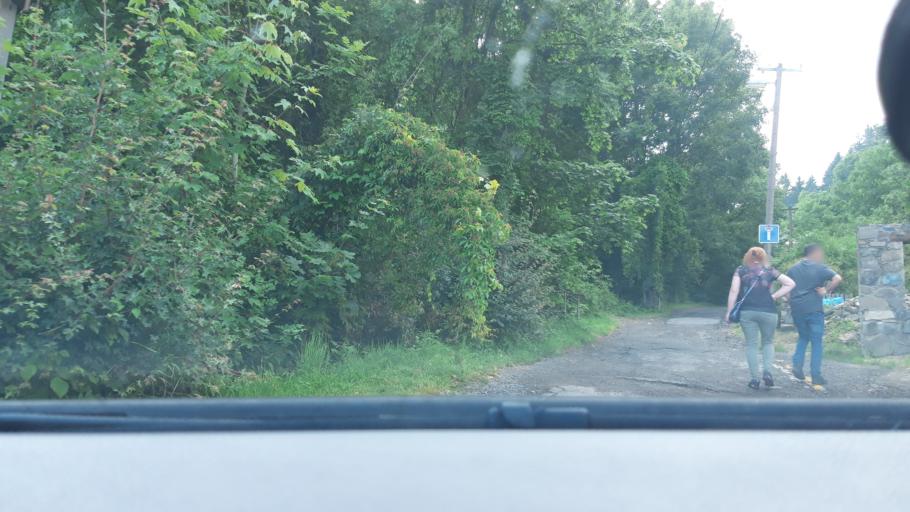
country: SK
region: Banskobystricky
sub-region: Okres Banska Bystrica
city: Banska Stiavnica
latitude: 48.4623
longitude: 18.8913
